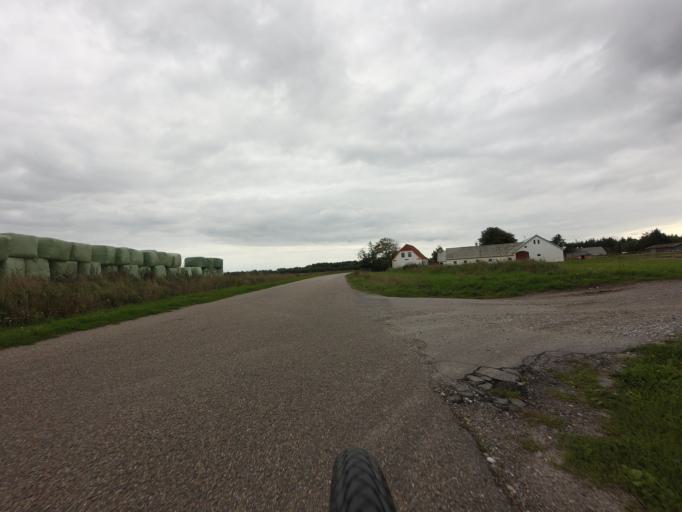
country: DK
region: North Denmark
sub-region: Hjorring Kommune
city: Hirtshals
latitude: 57.5712
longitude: 10.0312
